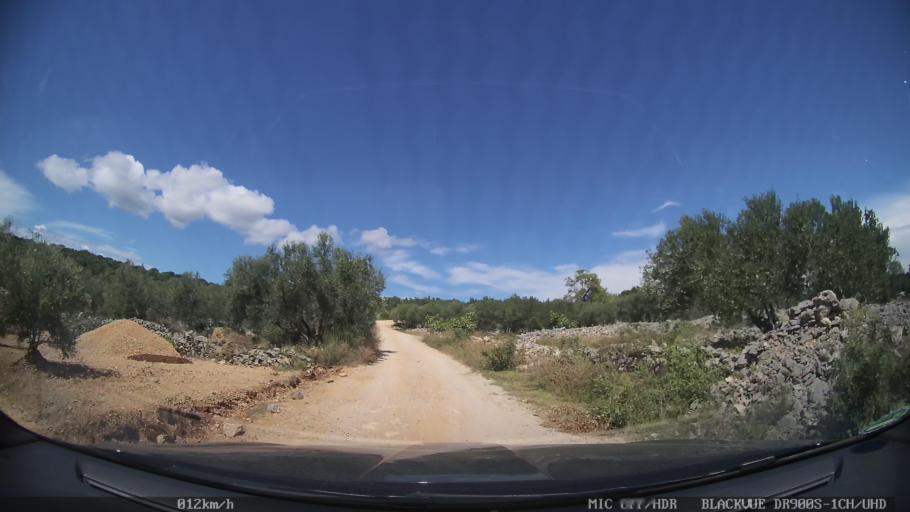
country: HR
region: Primorsko-Goranska
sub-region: Grad Krk
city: Krk
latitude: 45.0211
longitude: 14.5241
